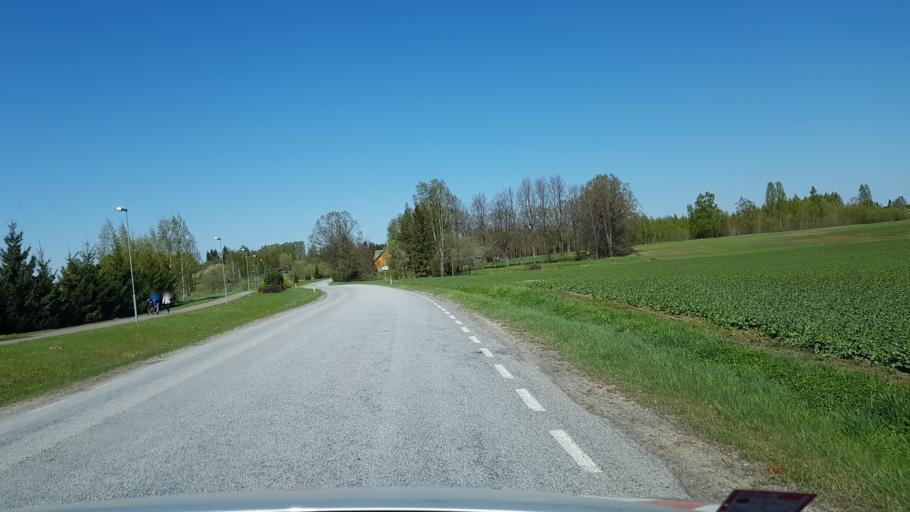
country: EE
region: Vorumaa
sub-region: Voru linn
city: Voru
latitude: 57.9002
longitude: 26.9952
